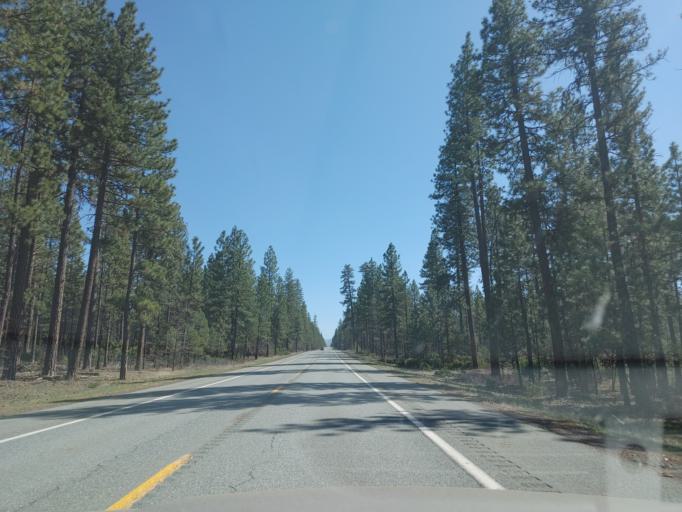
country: US
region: California
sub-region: Shasta County
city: Burney
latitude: 40.9801
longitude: -121.6230
